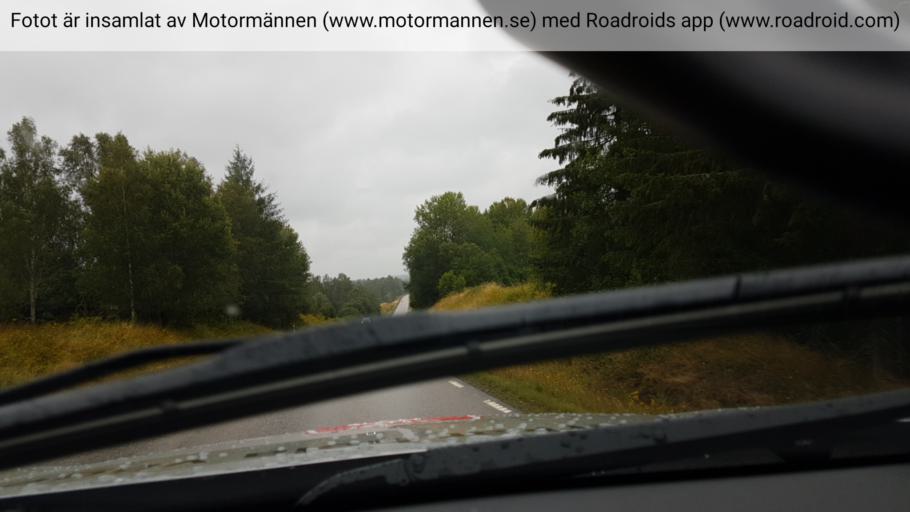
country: SE
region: Vaestra Goetaland
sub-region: Bengtsfors Kommun
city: Billingsfors
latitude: 58.9304
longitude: 12.2129
